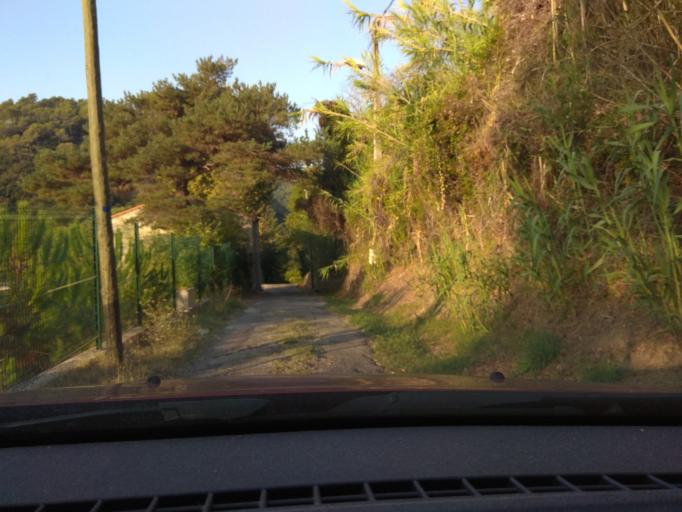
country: FR
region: Provence-Alpes-Cote d'Azur
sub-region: Departement des Alpes-Maritimes
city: La Colle-sur-Loup
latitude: 43.6853
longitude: 7.0958
